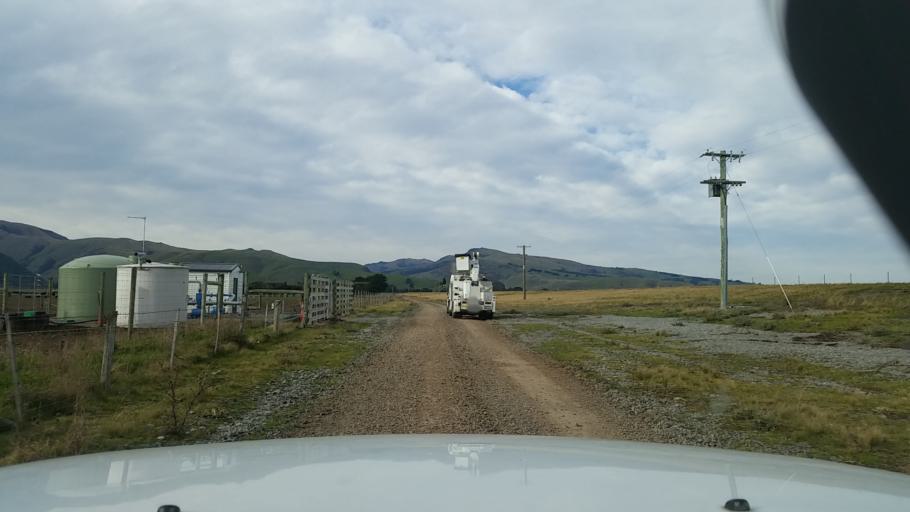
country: NZ
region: Canterbury
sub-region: Selwyn District
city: Lincoln
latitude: -43.8124
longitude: 172.6523
